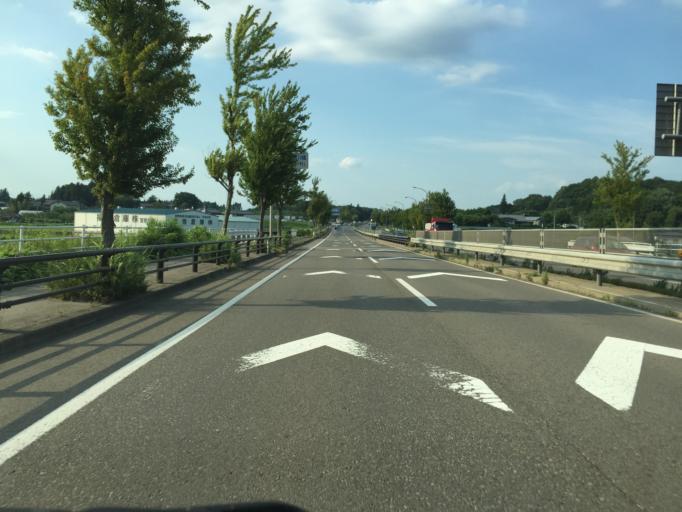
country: JP
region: Fukushima
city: Nihommatsu
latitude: 37.6325
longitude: 140.4819
